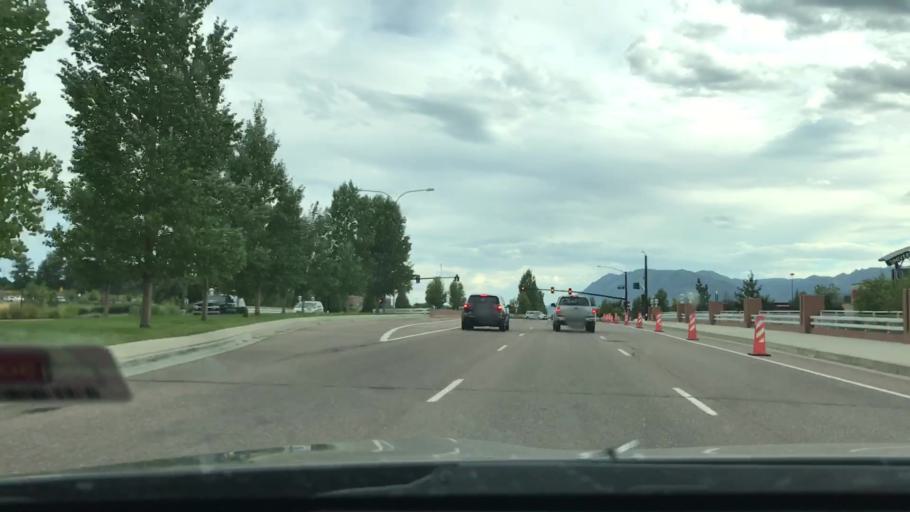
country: US
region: Colorado
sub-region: El Paso County
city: Colorado Springs
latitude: 38.9053
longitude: -104.8171
